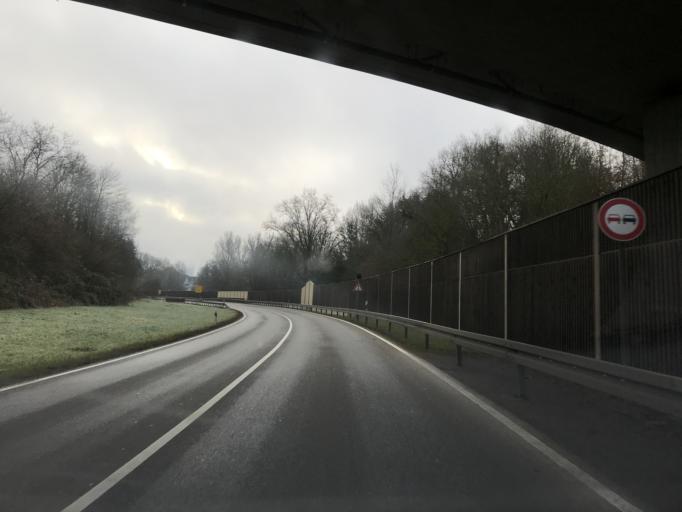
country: DE
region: Baden-Wuerttemberg
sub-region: Freiburg Region
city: Wehr
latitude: 47.6269
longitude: 7.8974
